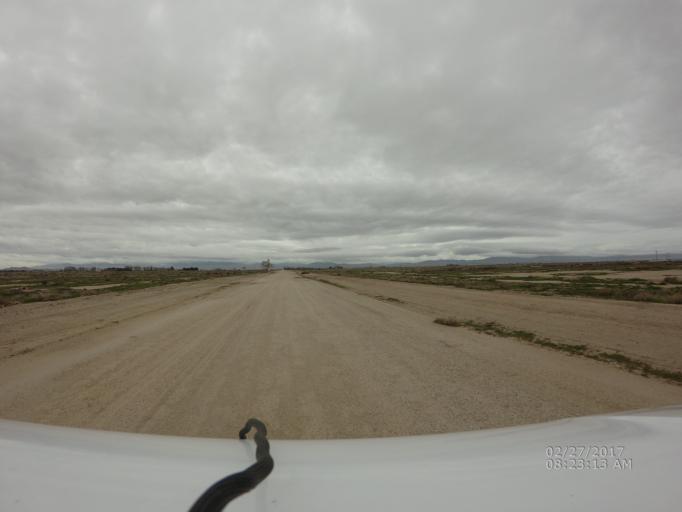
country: US
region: California
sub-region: Los Angeles County
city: Lancaster
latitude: 34.7280
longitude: -118.0143
